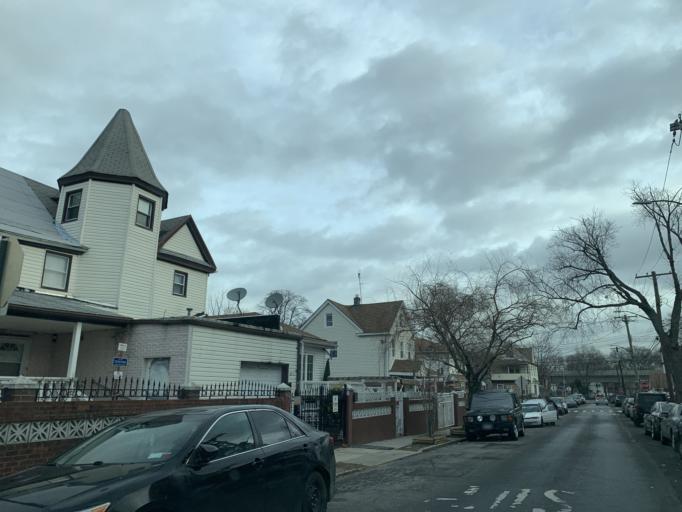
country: US
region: New York
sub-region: Queens County
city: Jamaica
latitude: 40.6902
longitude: -73.8119
